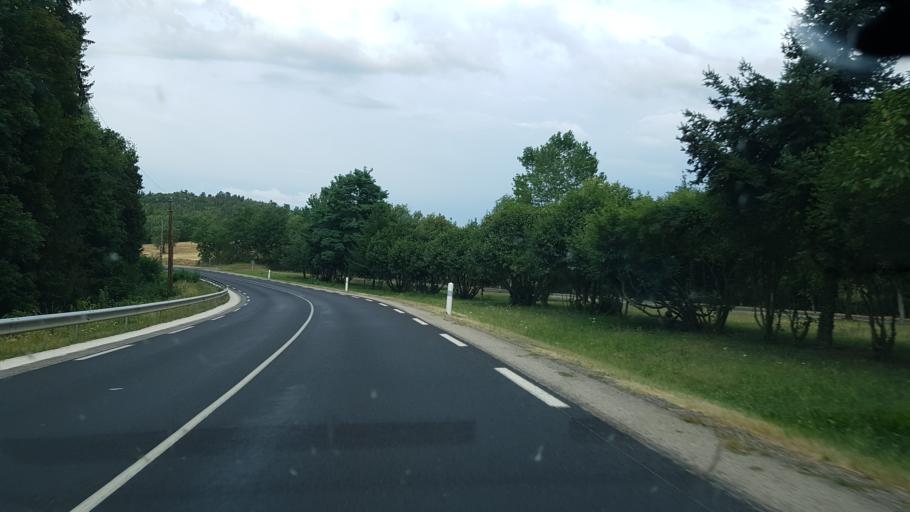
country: FR
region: Auvergne
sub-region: Departement de la Haute-Loire
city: Vieille-Brioude
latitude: 45.2743
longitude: 3.3393
